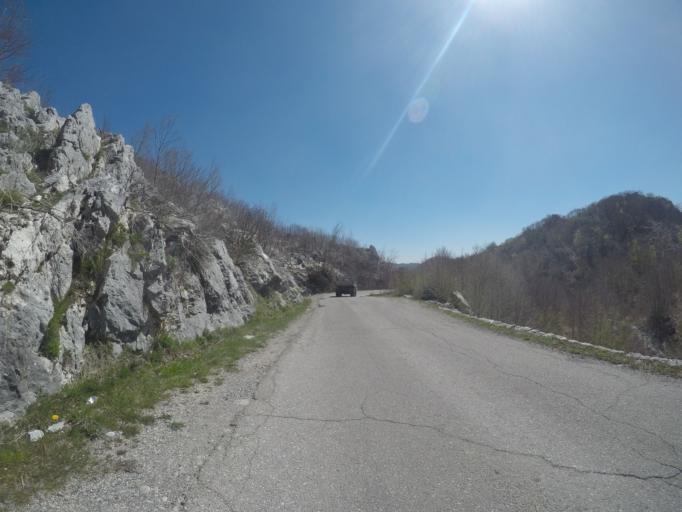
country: ME
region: Cetinje
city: Cetinje
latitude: 42.4357
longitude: 18.8602
